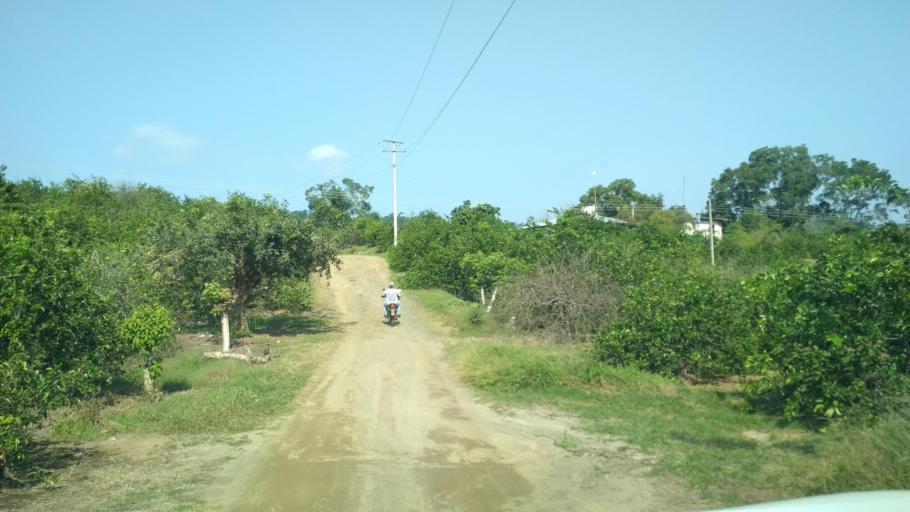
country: MX
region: Puebla
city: San Jose Acateno
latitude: 20.1707
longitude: -97.1737
